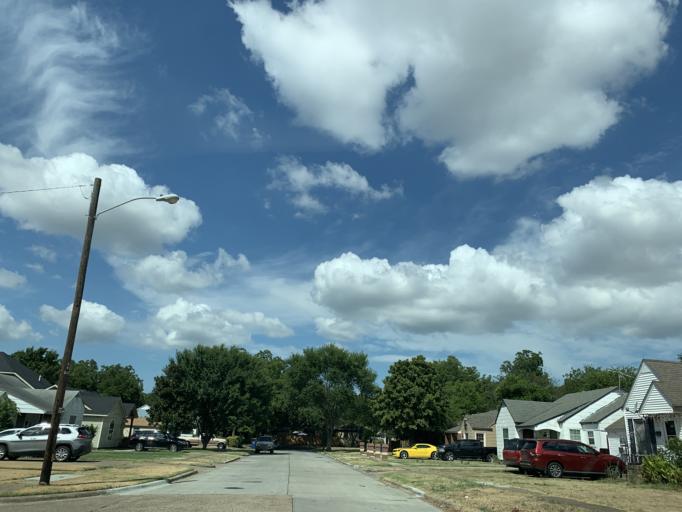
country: US
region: Texas
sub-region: Dallas County
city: Cockrell Hill
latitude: 32.7372
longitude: -96.8602
